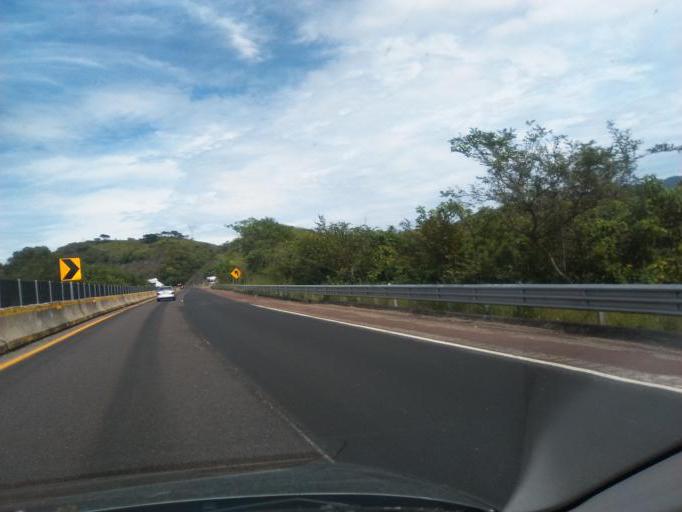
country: MX
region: Guerrero
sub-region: Chilpancingo de los Bravo
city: Acahuizotla
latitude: 17.3720
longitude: -99.4794
